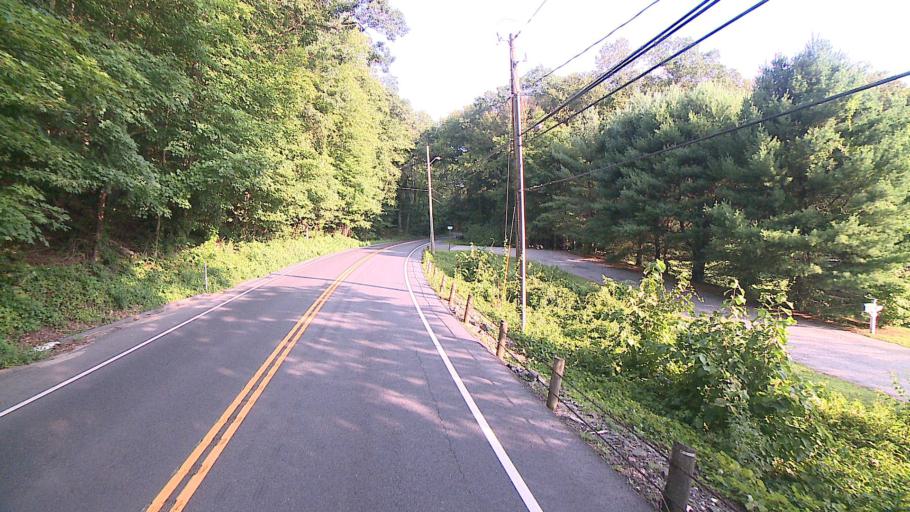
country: US
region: Connecticut
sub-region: Fairfield County
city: Sherman
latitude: 41.6132
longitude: -73.4523
